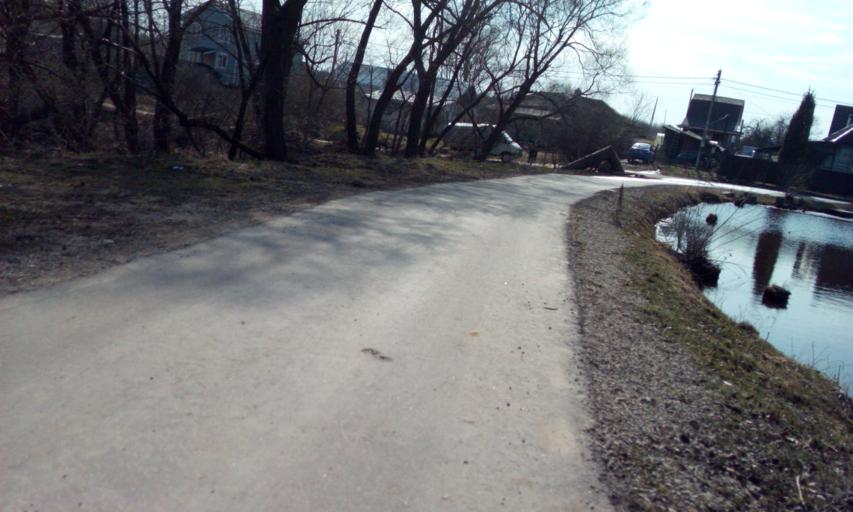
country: RU
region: Moskovskaya
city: Vatutinki
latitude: 55.4582
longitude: 37.3808
